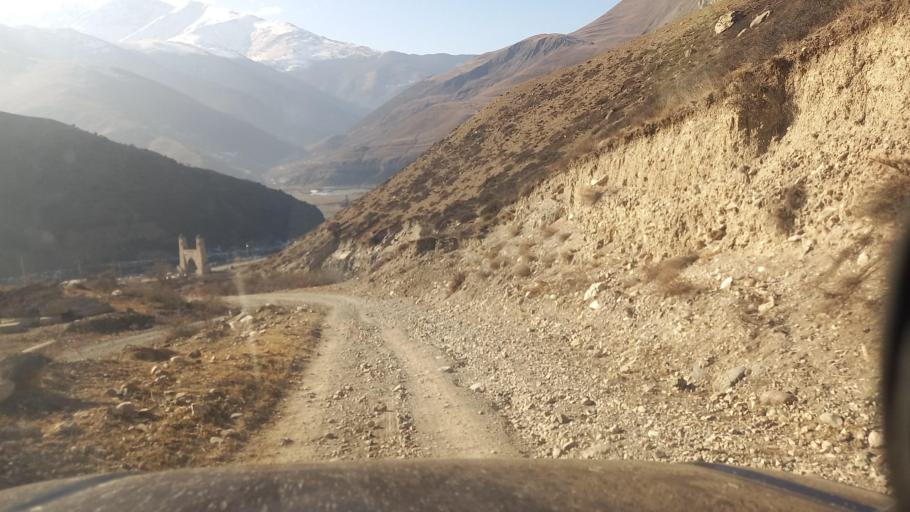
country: RU
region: Ingushetiya
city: Dzhayrakh
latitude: 42.8459
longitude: 44.6521
